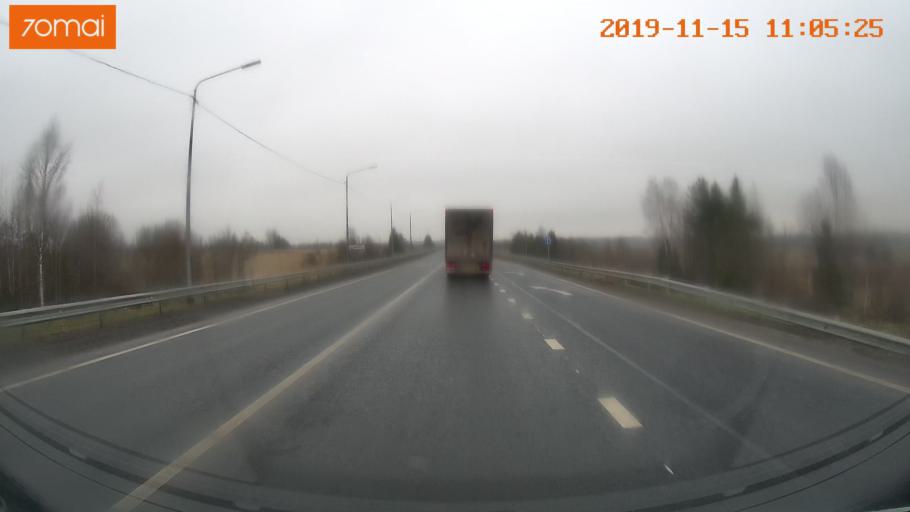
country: RU
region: Vologda
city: Chebsara
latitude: 59.1185
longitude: 39.0038
